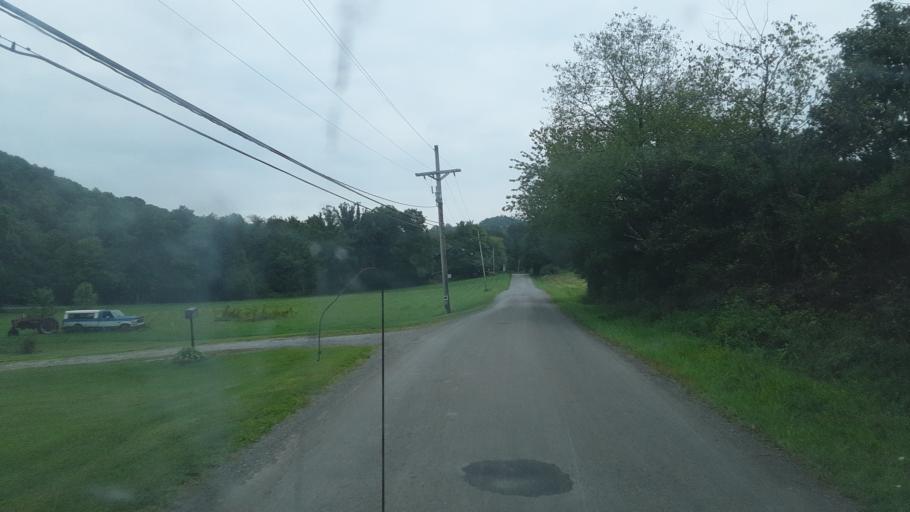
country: US
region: Pennsylvania
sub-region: Jefferson County
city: Punxsutawney
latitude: 40.9702
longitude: -79.1336
